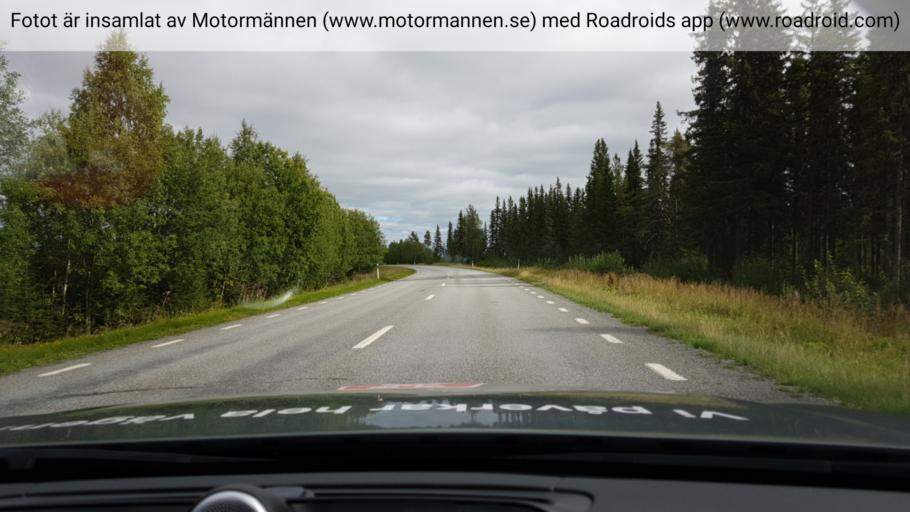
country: SE
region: Jaemtland
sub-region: Stroemsunds Kommun
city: Stroemsund
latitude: 63.5078
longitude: 15.2789
